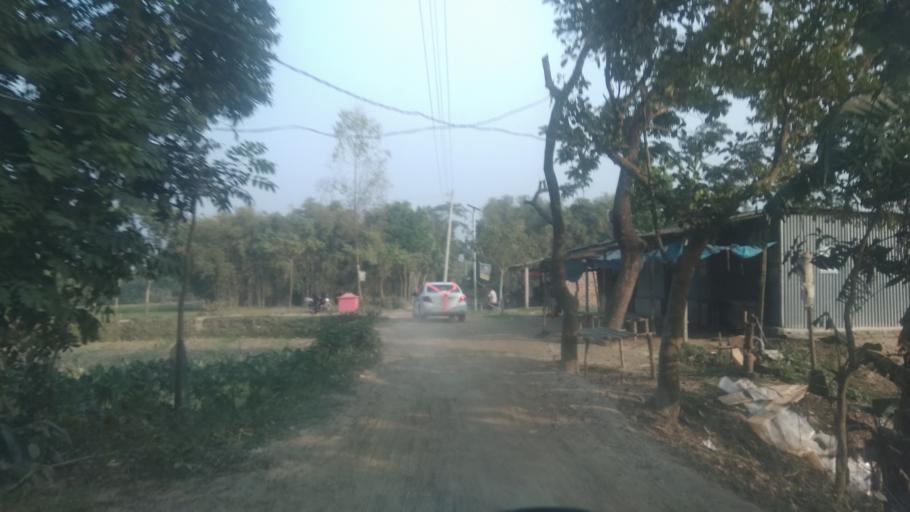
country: BD
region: Dhaka
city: Netrakona
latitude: 24.7743
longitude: 90.6095
